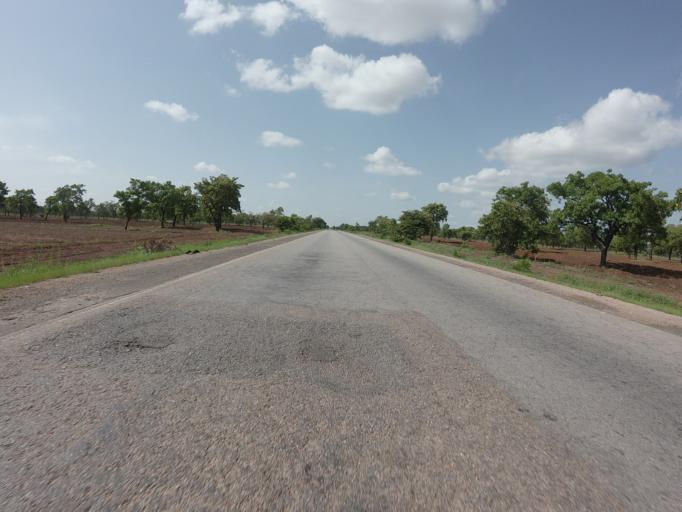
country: GH
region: Northern
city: Savelugu
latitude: 9.9606
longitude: -0.8326
